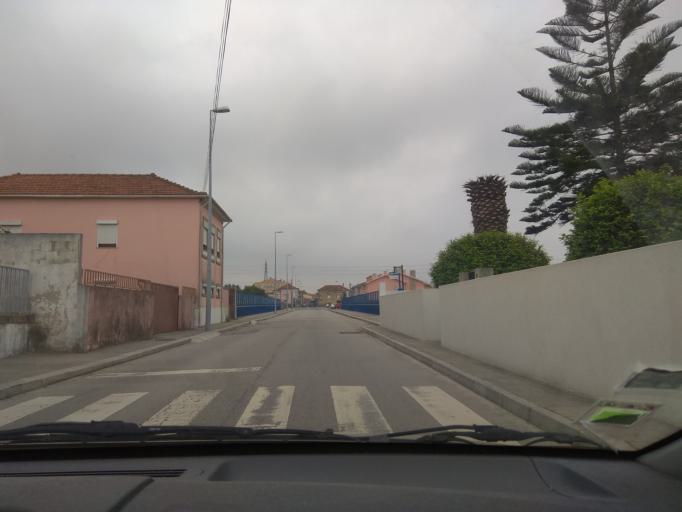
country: PT
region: Porto
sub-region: Matosinhos
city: Guifoes
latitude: 41.1973
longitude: -8.6640
